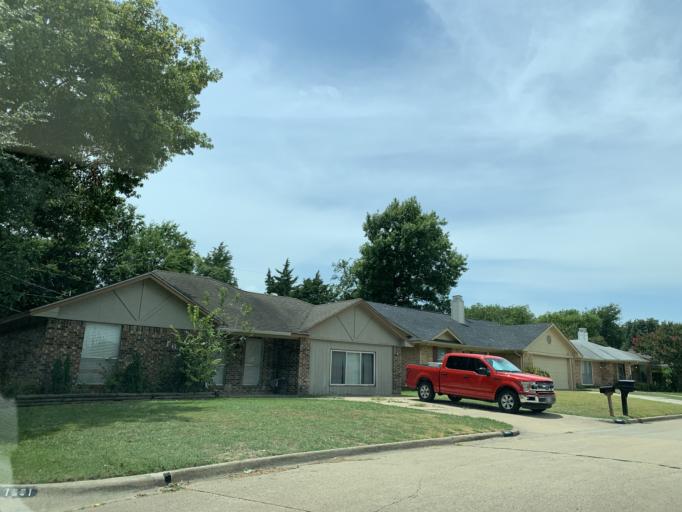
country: US
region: Texas
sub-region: Dallas County
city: Grand Prairie
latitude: 32.6635
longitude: -97.0244
